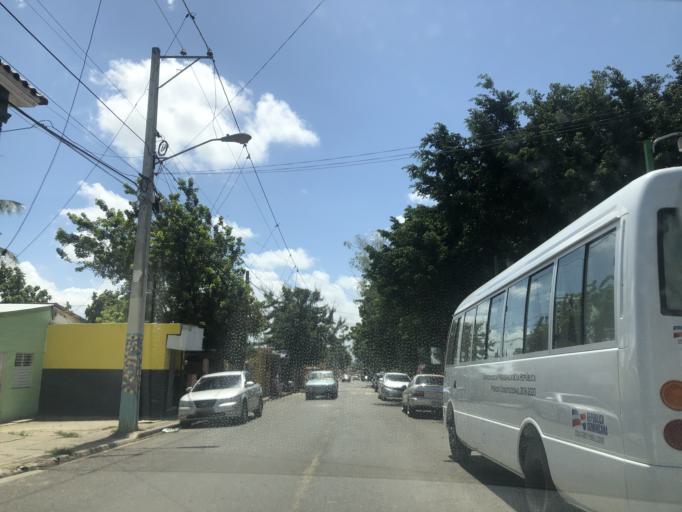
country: DO
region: Santiago
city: La Canela
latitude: 19.4508
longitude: -70.7805
